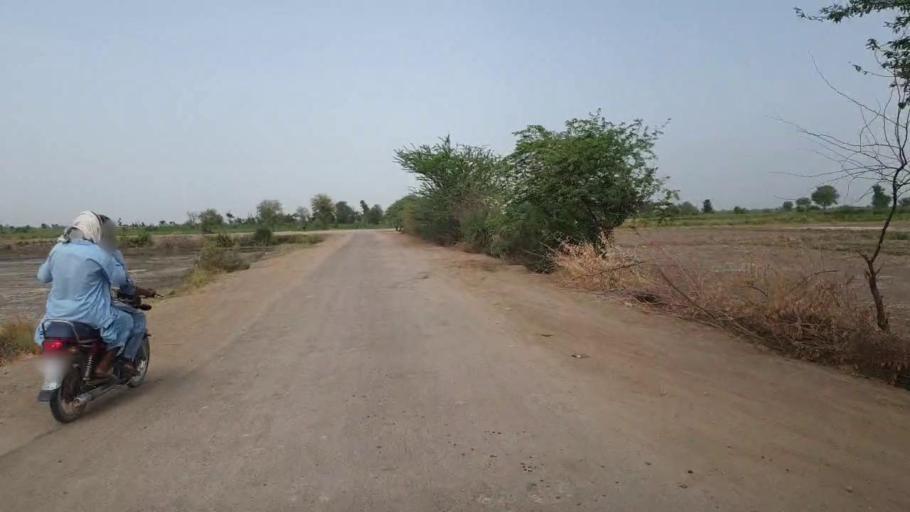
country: PK
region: Sindh
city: Daulatpur
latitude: 26.5462
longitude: 68.0881
